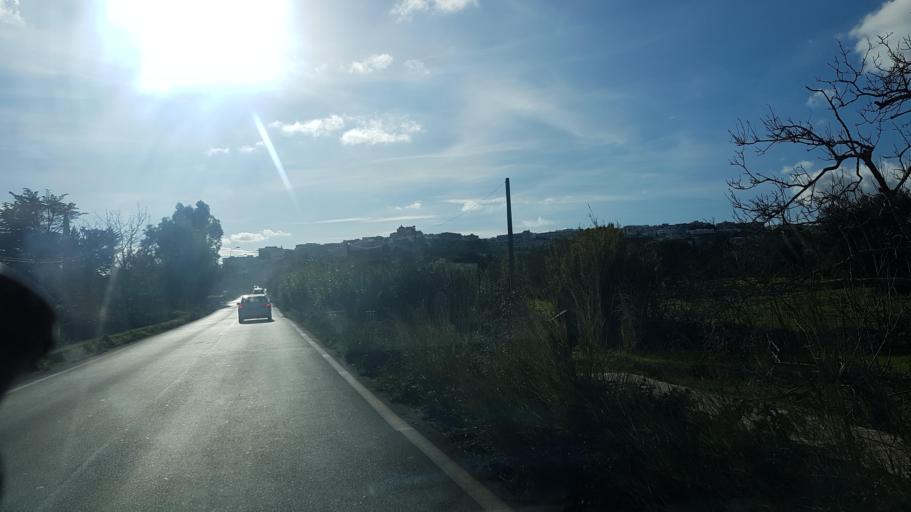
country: IT
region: Apulia
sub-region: Provincia di Brindisi
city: Ceglie Messapica
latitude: 40.6531
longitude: 17.5252
